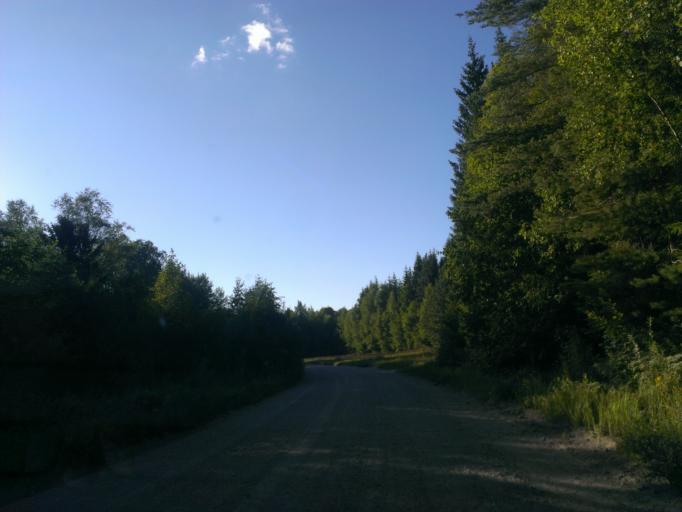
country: LV
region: Malpils
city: Malpils
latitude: 57.1007
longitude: 25.0417
